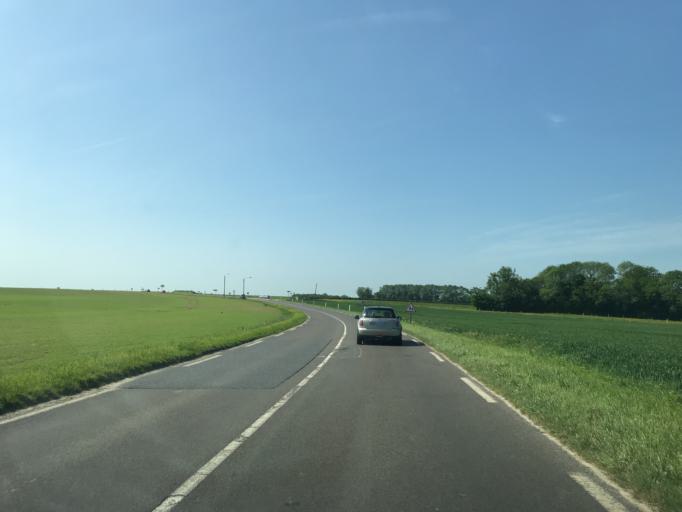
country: FR
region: Haute-Normandie
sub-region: Departement de la Seine-Maritime
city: Belbeuf
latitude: 49.3798
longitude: 1.1624
